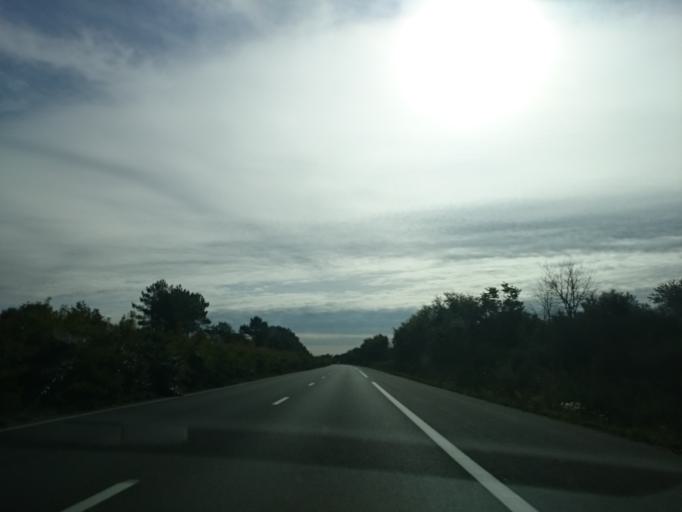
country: FR
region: Pays de la Loire
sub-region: Departement de la Loire-Atlantique
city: La Chapelle-des-Marais
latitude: 47.4909
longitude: -2.2358
